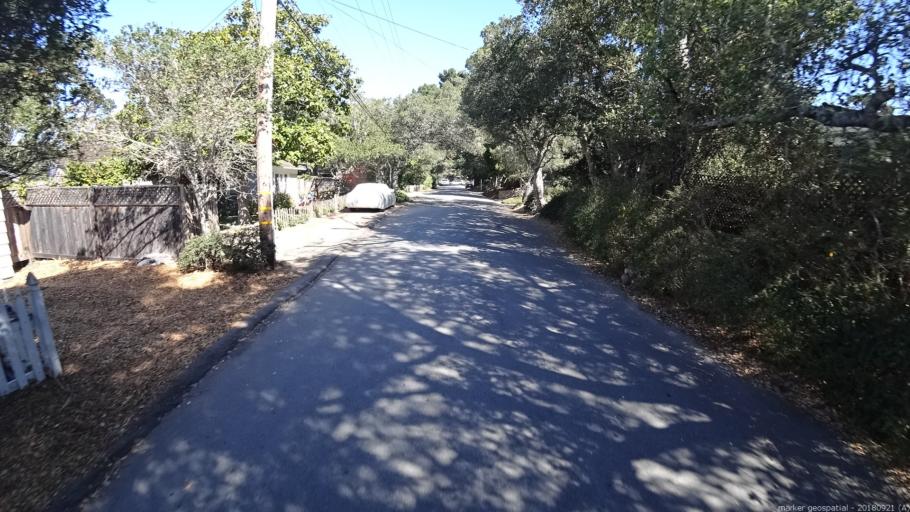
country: US
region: California
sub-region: Monterey County
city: Carmel-by-the-Sea
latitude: 36.5572
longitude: -121.9150
